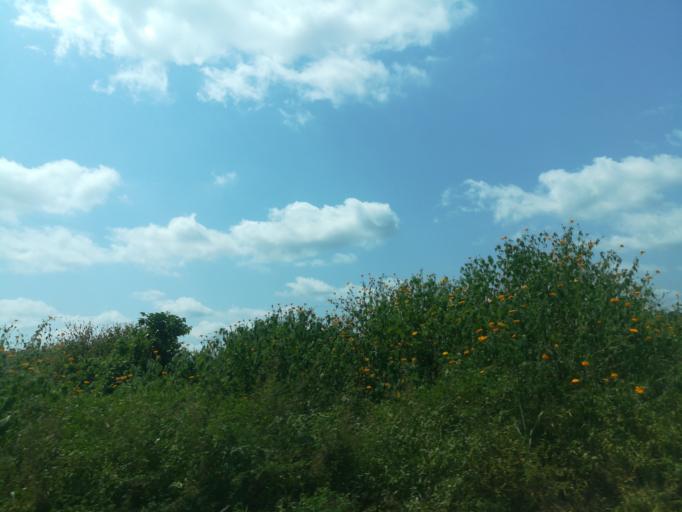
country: NG
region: Oyo
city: Moniya
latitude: 7.5772
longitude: 3.9109
